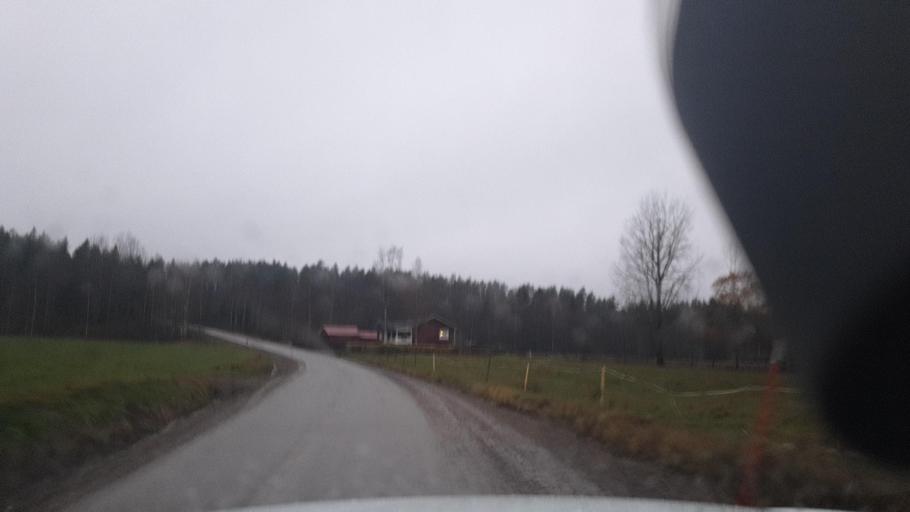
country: SE
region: Vaermland
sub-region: Eda Kommun
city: Charlottenberg
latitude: 59.7289
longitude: 12.1382
